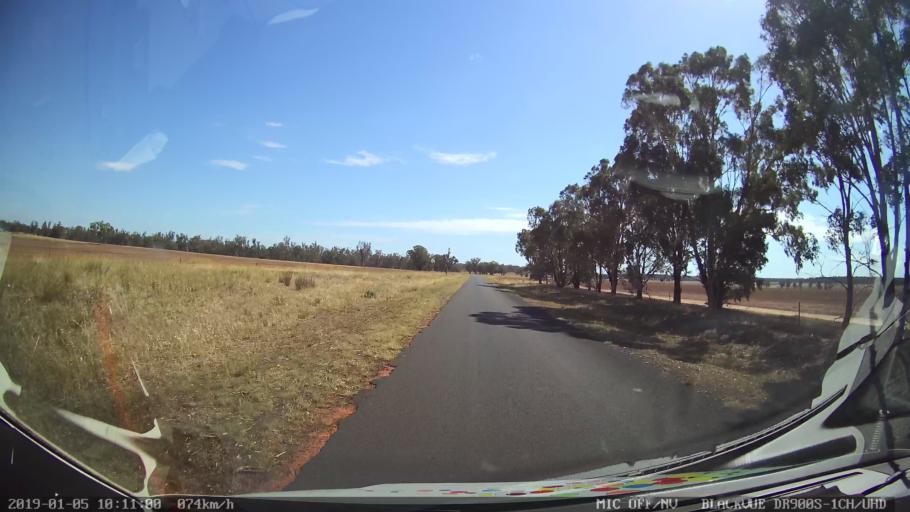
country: AU
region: New South Wales
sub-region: Gilgandra
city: Gilgandra
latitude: -31.6167
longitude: 148.8971
